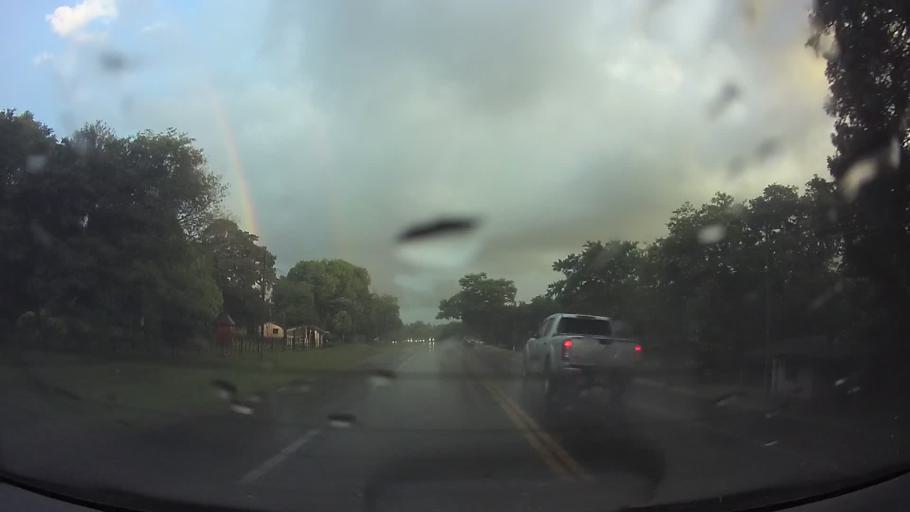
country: PY
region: Paraguari
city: Paraguari
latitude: -25.5947
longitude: -57.2174
